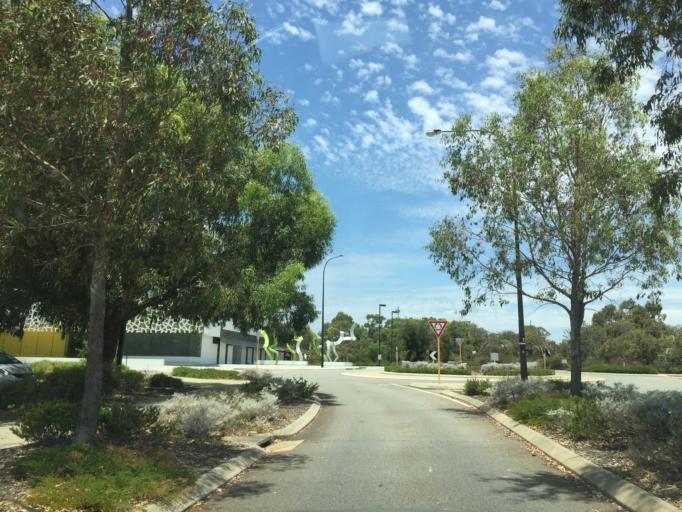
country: AU
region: Western Australia
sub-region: Melville
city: Winthrop
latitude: -32.0729
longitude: 115.8451
